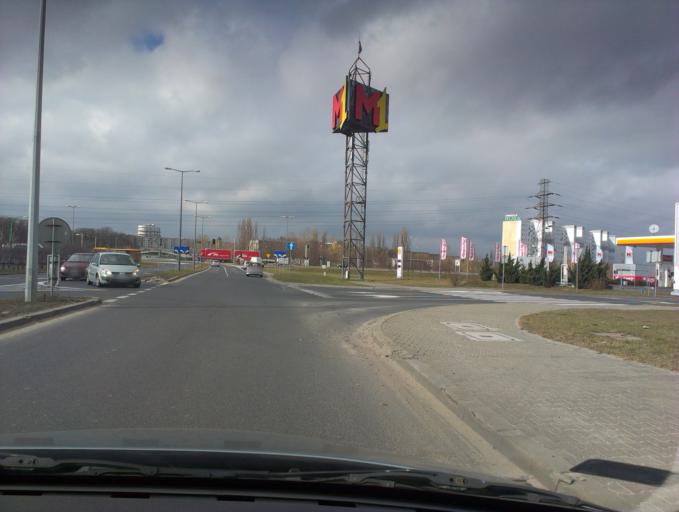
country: PL
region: Greater Poland Voivodeship
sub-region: Poznan
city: Poznan
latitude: 52.3833
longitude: 16.9901
